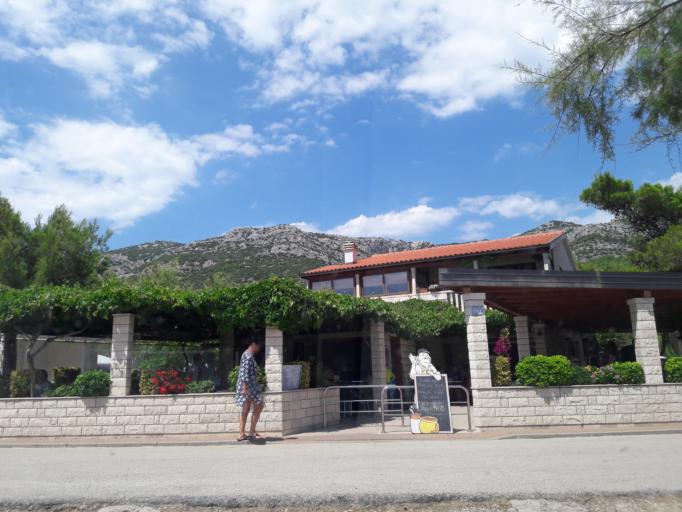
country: HR
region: Dubrovacko-Neretvanska
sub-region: Grad Korcula
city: Zrnovo
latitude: 42.9791
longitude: 17.1036
